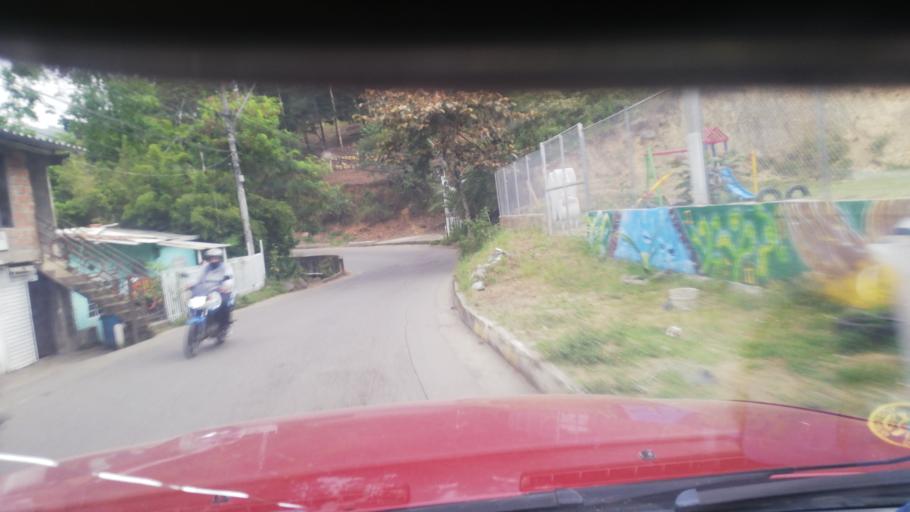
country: CO
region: Valle del Cauca
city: Cali
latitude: 3.4784
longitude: -76.5534
